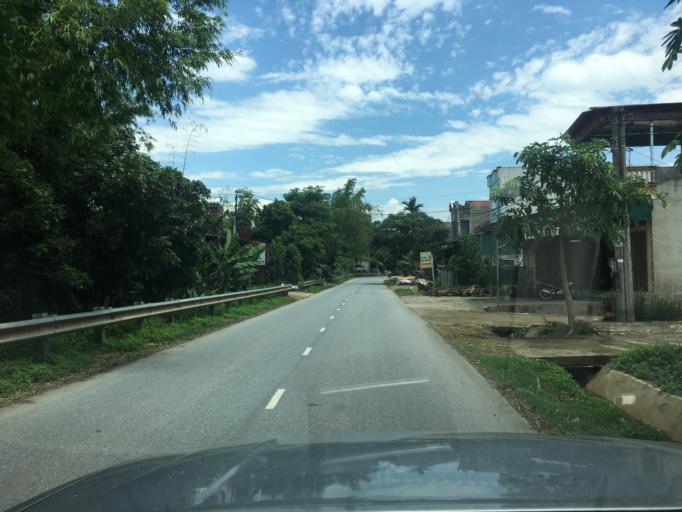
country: VN
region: Yen Bai
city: Son Thinh
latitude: 21.6543
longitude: 104.5008
